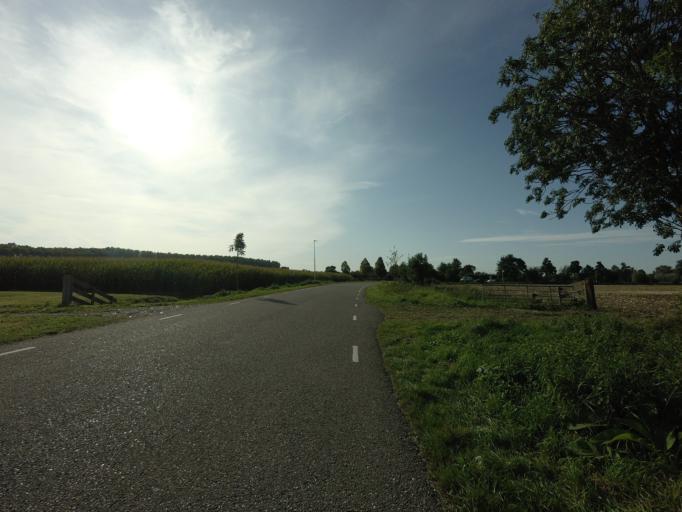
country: NL
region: Utrecht
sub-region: Gemeente Lopik
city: Lopik
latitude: 51.9432
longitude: 4.9699
